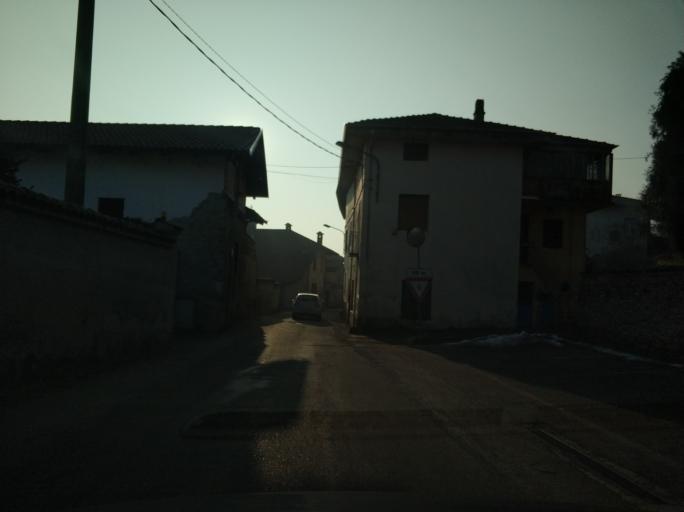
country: IT
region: Piedmont
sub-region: Provincia di Torino
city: Front
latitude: 45.2817
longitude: 7.6622
